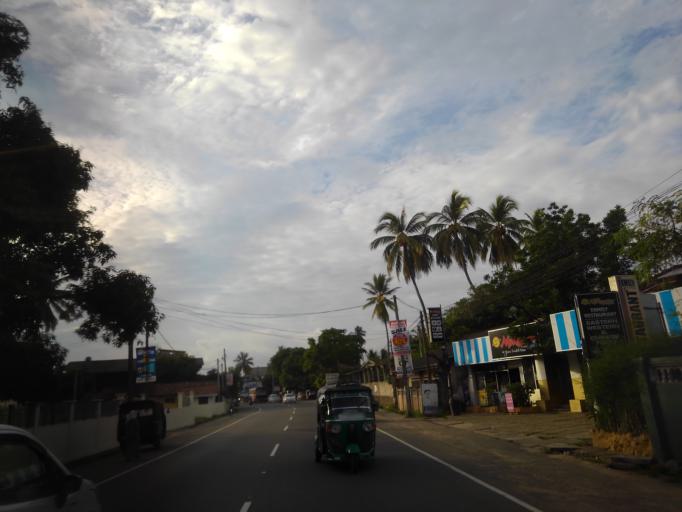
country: LK
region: Southern
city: Galle
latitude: 6.0347
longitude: 80.2341
